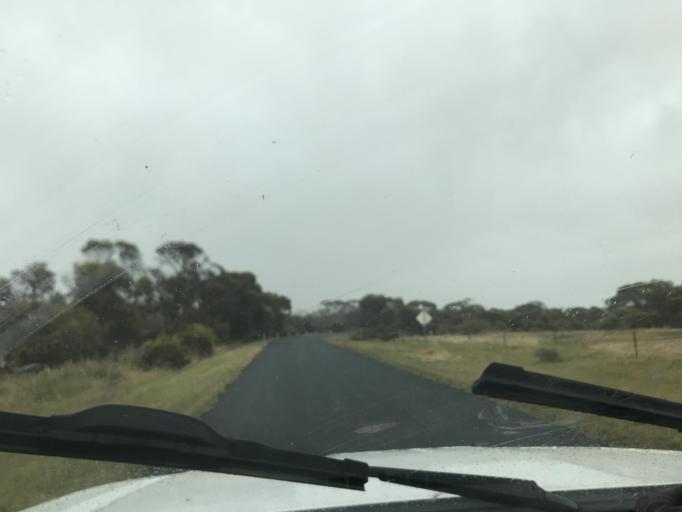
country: AU
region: South Australia
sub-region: Tatiara
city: Bordertown
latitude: -36.3185
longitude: 141.1869
